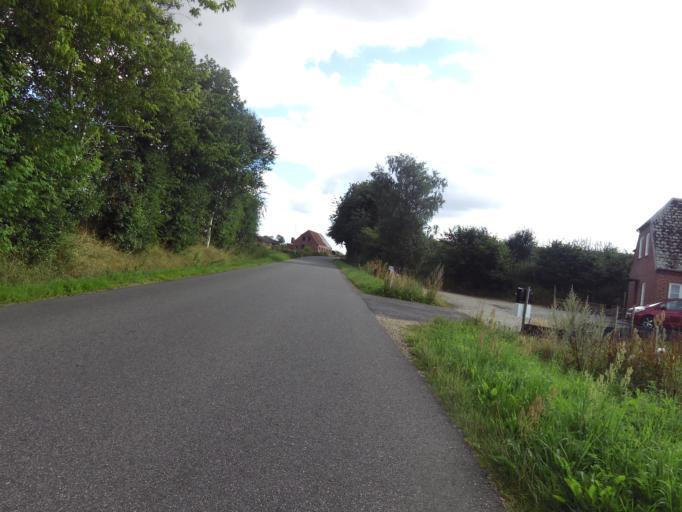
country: DK
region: South Denmark
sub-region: Haderslev Kommune
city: Haderslev
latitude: 55.2378
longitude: 9.4682
